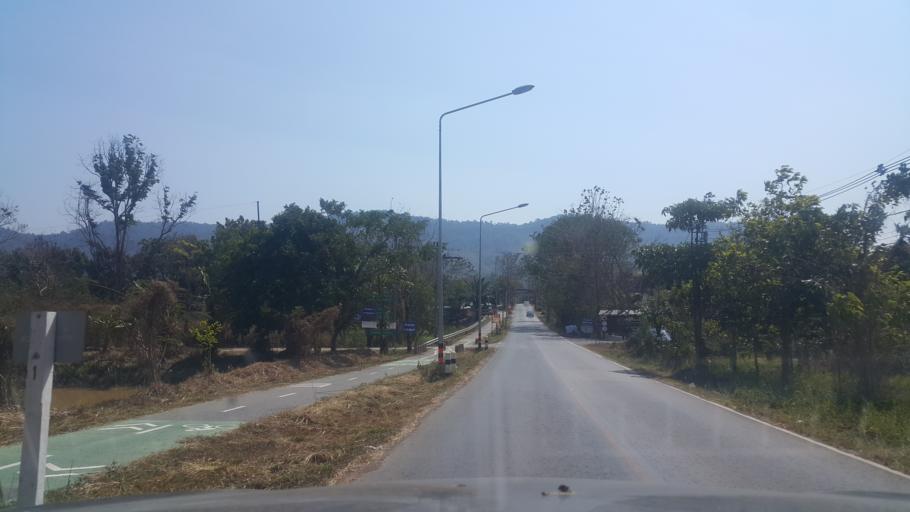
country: TH
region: Nakhon Ratchasima
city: Wang Nam Khiao
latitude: 14.3494
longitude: 101.9383
